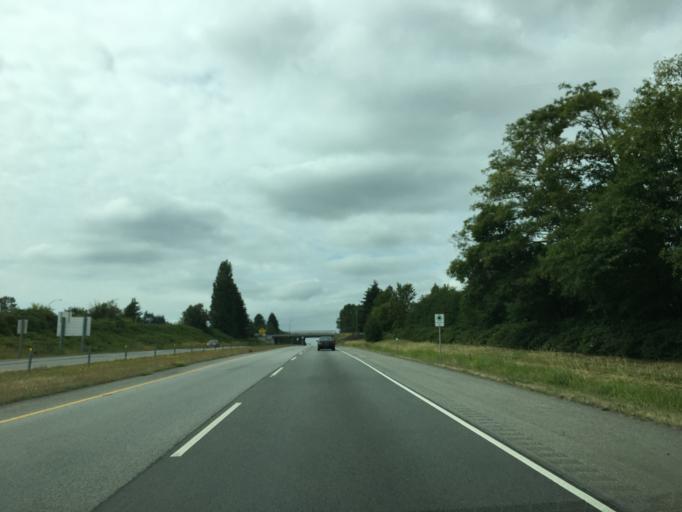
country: CA
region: British Columbia
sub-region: Greater Vancouver Regional District
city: White Rock
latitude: 49.0429
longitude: -122.7822
